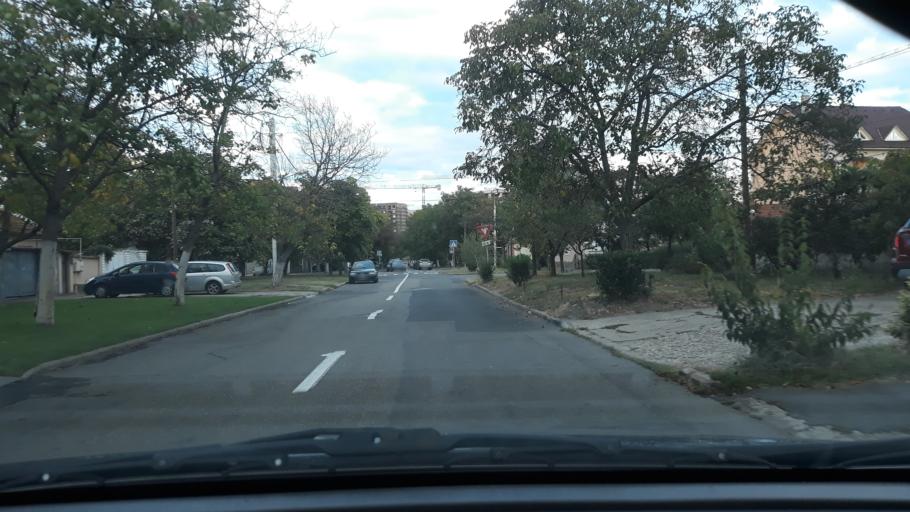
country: RO
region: Bihor
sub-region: Comuna Biharea
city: Oradea
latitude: 47.0591
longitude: 21.9049
